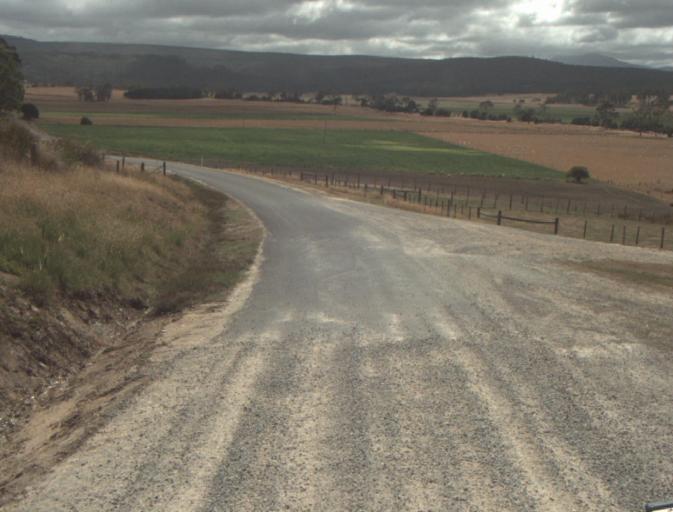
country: AU
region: Tasmania
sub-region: Northern Midlands
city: Evandale
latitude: -41.4870
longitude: 147.4389
